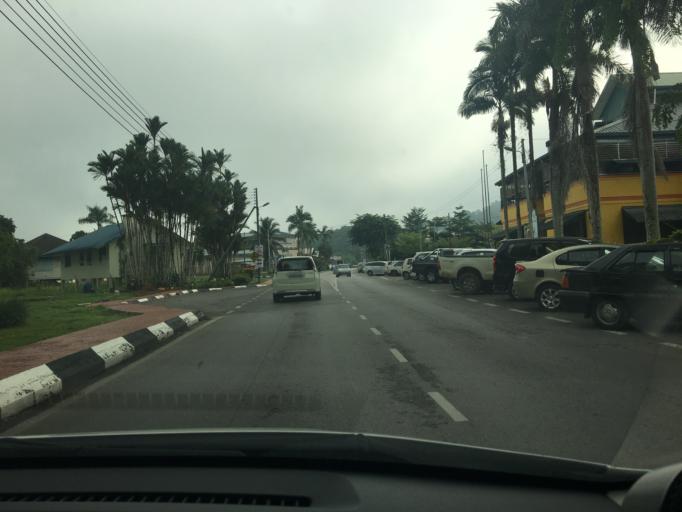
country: MY
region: Sarawak
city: Kuching
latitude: 1.4167
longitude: 110.1540
